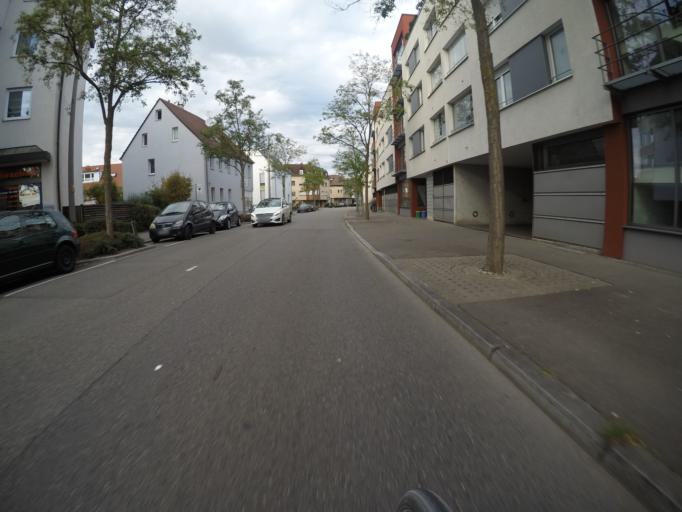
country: DE
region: Baden-Wuerttemberg
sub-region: Regierungsbezirk Stuttgart
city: Boeblingen
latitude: 48.6873
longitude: 9.0159
